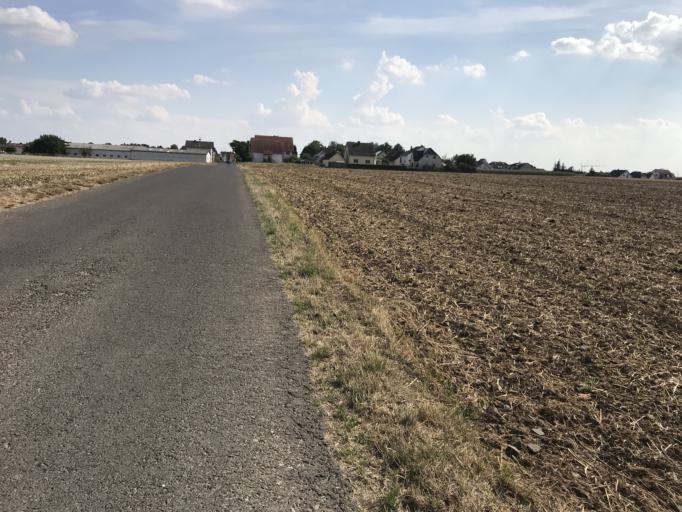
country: DE
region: Hesse
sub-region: Regierungsbezirk Darmstadt
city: Wolfersheim
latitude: 50.3680
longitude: 8.8222
